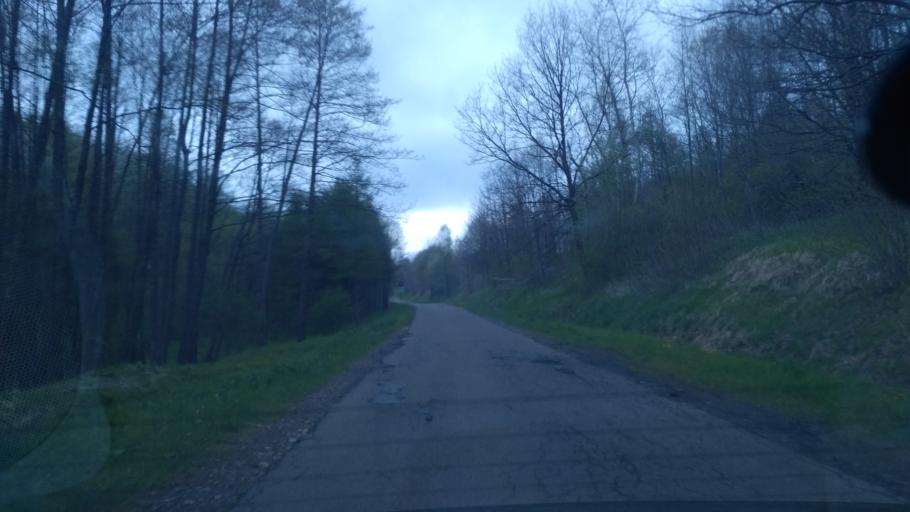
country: PL
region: Subcarpathian Voivodeship
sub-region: Powiat sanocki
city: Sanok
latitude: 49.6418
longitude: 22.2717
